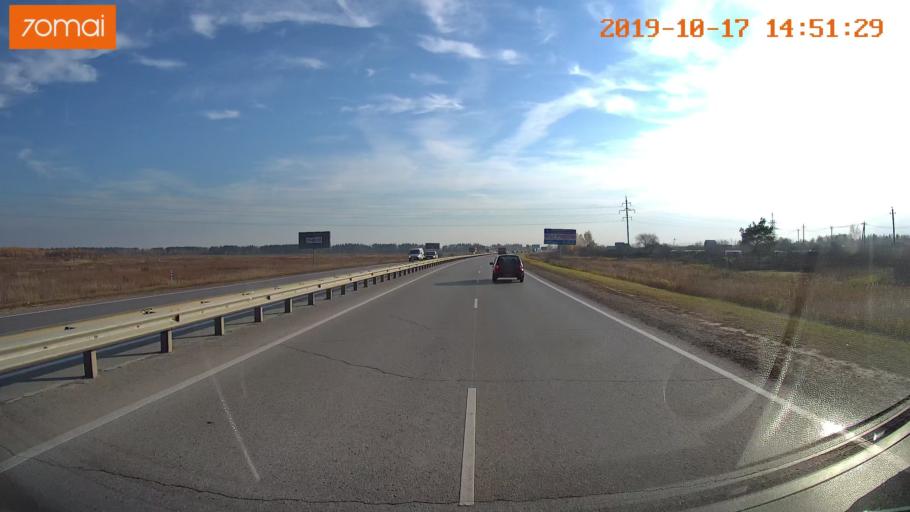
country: RU
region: Rjazan
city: Polyany
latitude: 54.7181
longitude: 39.8482
